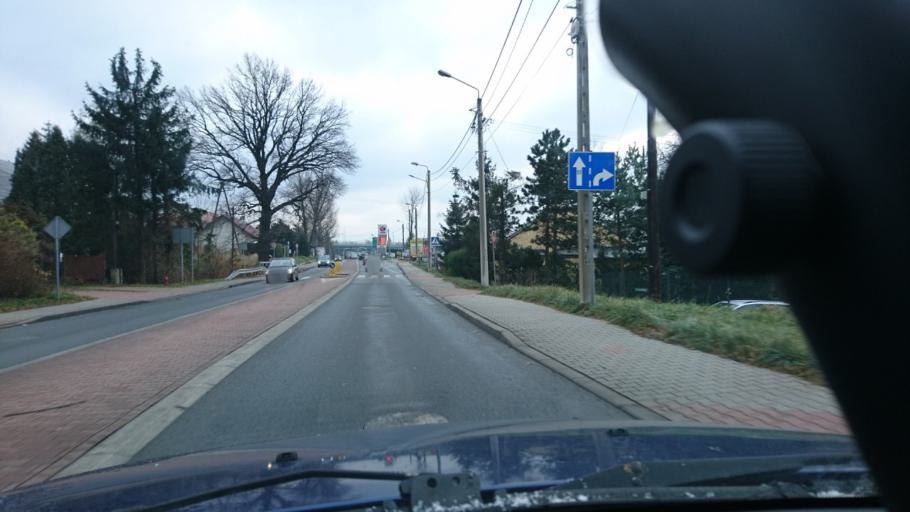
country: PL
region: Silesian Voivodeship
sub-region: Powiat bielski
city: Bystra
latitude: 49.7915
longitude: 19.0685
